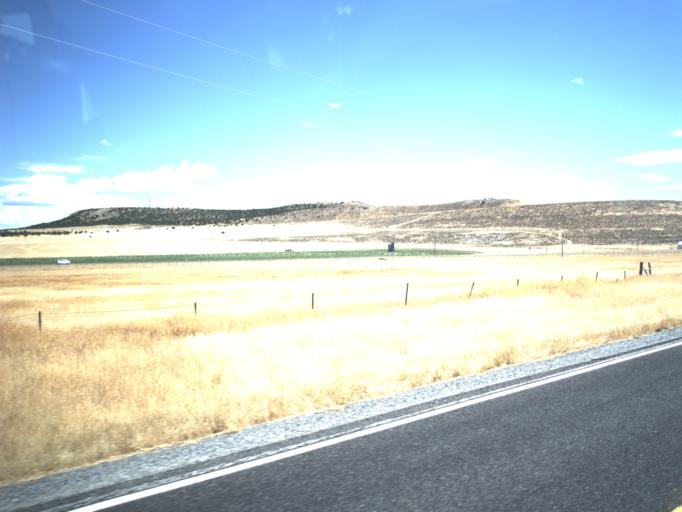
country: US
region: Idaho
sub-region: Oneida County
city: Malad City
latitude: 41.9661
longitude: -112.7693
